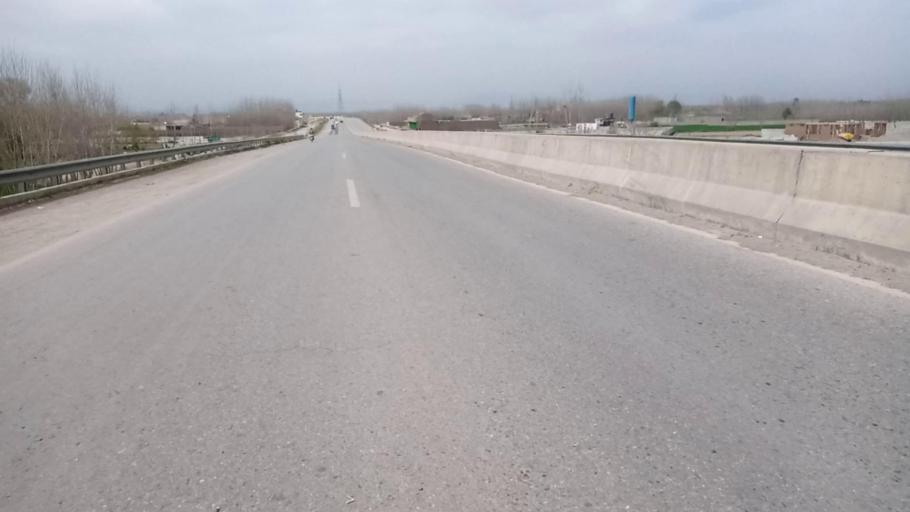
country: PK
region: Khyber Pakhtunkhwa
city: Peshawar
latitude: 34.0496
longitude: 71.6143
